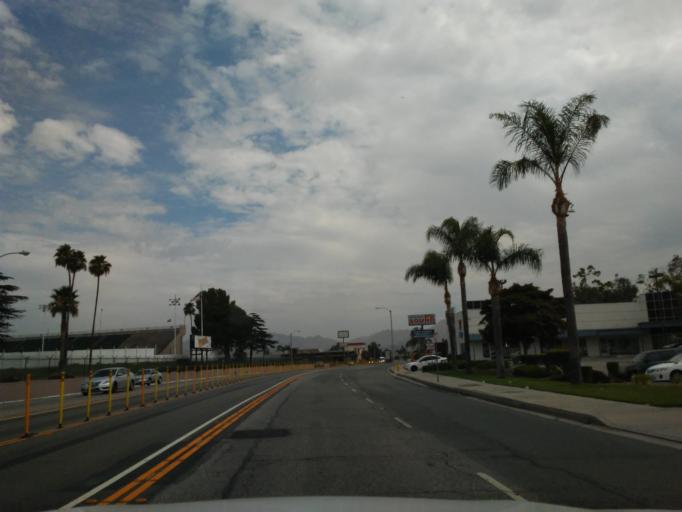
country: US
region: California
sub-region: San Bernardino County
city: San Bernardino
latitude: 34.0879
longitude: -117.2941
